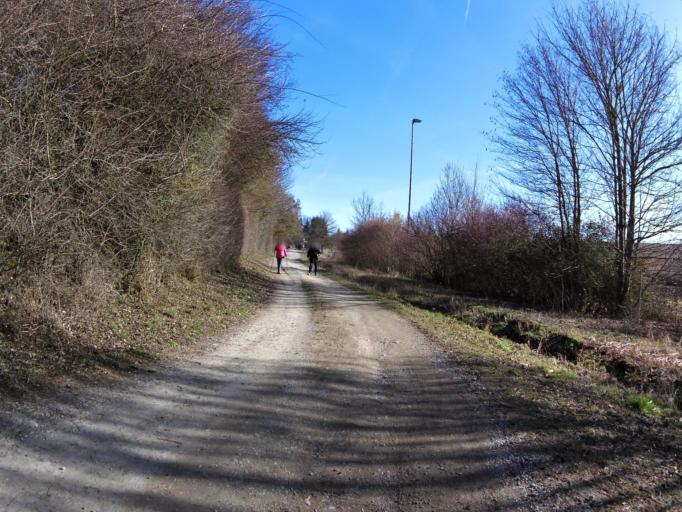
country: DE
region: Bavaria
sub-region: Regierungsbezirk Unterfranken
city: Rimpar
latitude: 49.8505
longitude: 9.9836
